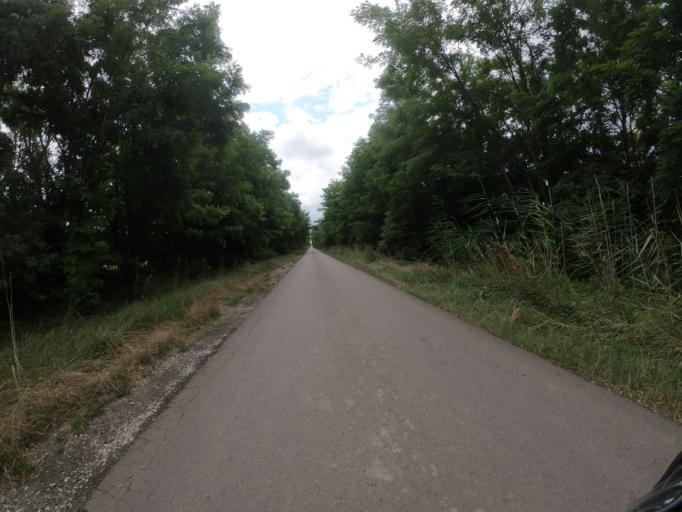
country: HU
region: Borsod-Abauj-Zemplen
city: Szentistvan
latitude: 47.7238
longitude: 20.6864
